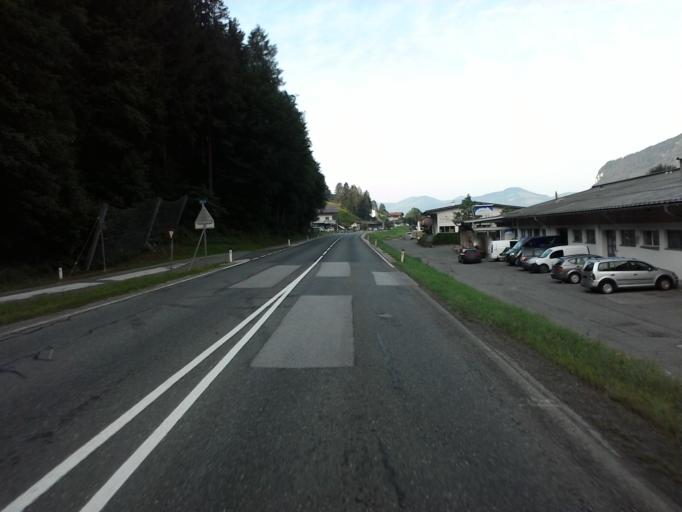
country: AT
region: Tyrol
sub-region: Politischer Bezirk Kitzbuhel
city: Kirchdorf in Tirol
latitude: 47.5580
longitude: 12.4598
